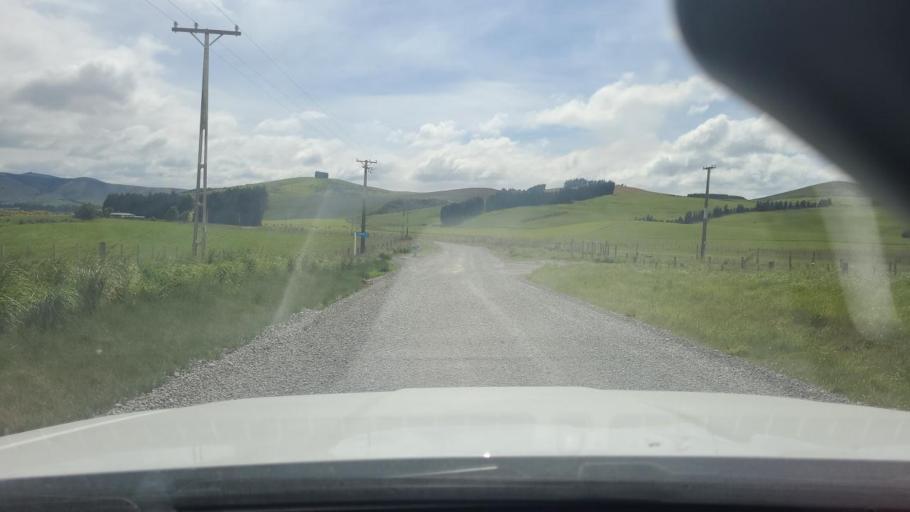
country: NZ
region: Southland
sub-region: Southland District
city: Te Anau
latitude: -45.5076
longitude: 167.8837
